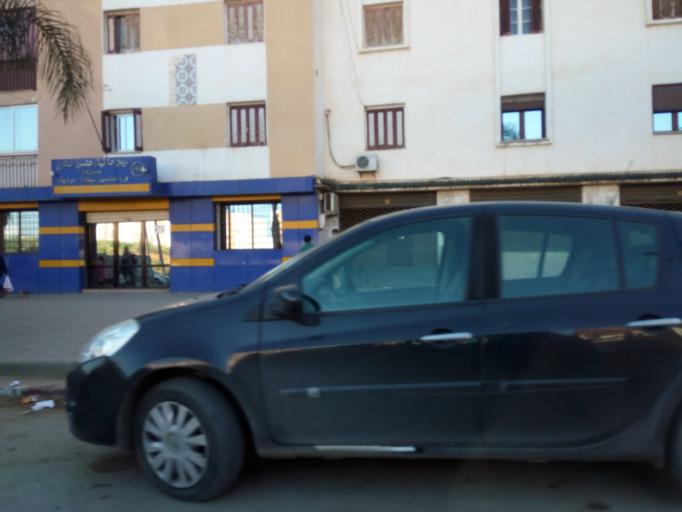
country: DZ
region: Tipaza
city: Saoula
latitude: 36.7161
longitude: 3.0125
